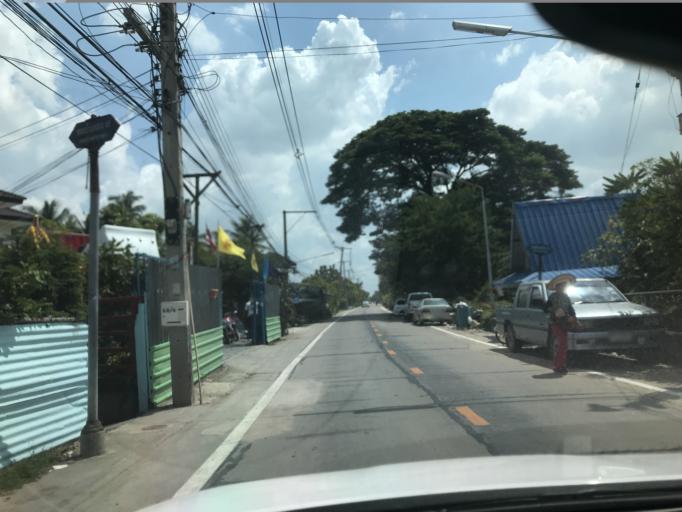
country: TH
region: Pathum Thani
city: Pathum Thani
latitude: 14.0147
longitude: 100.5392
